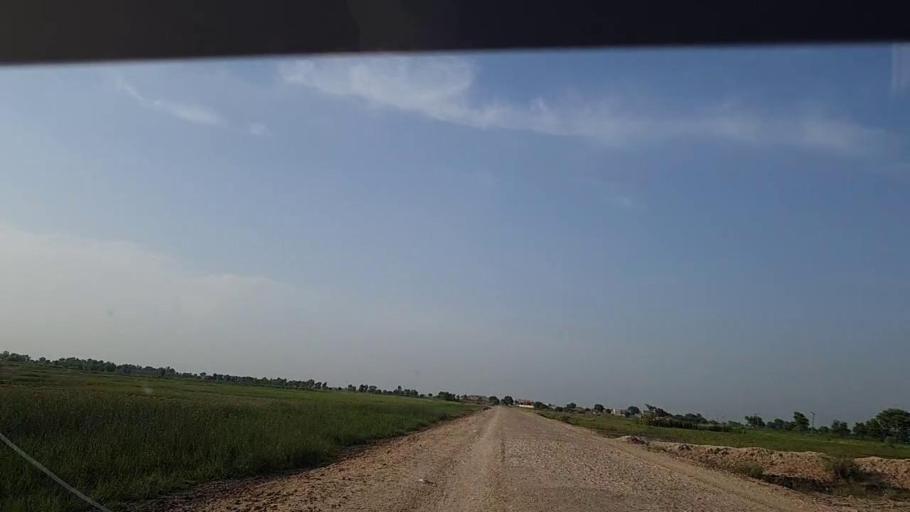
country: PK
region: Sindh
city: Khanpur
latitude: 27.8324
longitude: 69.3742
